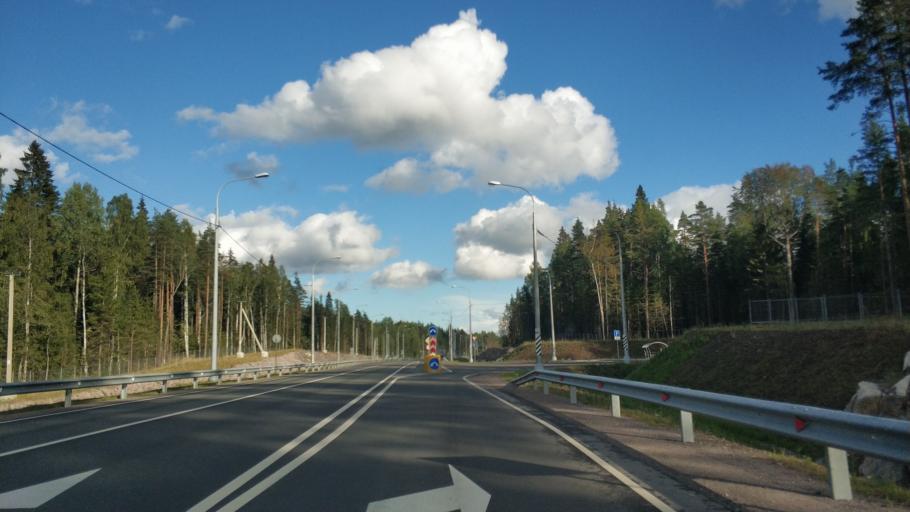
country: RU
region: Leningrad
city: Kuznechnoye
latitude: 61.0948
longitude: 29.9878
